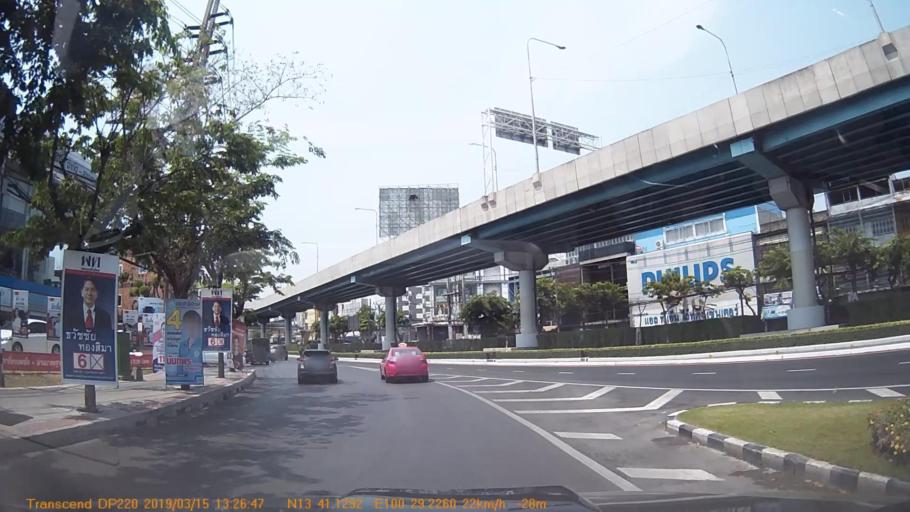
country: TH
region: Bangkok
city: Chom Thong
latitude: 13.6855
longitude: 100.4871
